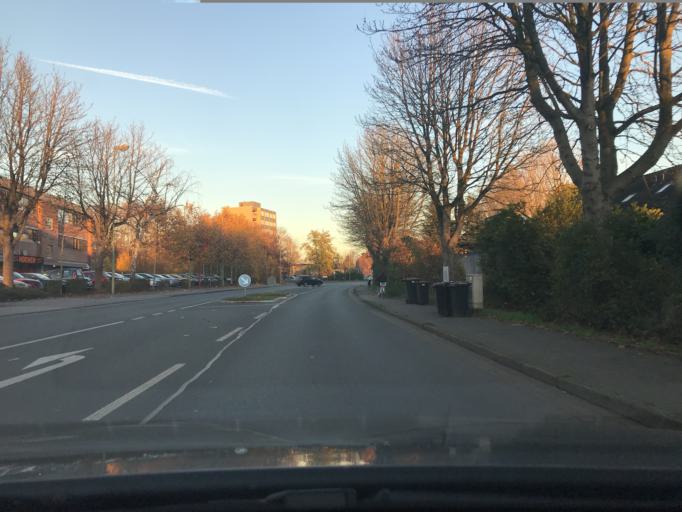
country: DE
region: North Rhine-Westphalia
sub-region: Regierungsbezirk Dusseldorf
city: Moers
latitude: 51.4466
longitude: 6.5712
